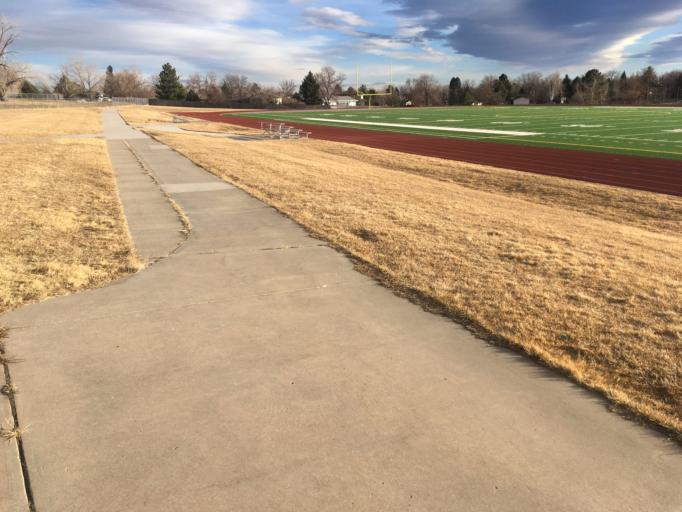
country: US
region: Colorado
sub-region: Broomfield County
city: Broomfield
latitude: 39.9371
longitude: -105.0795
